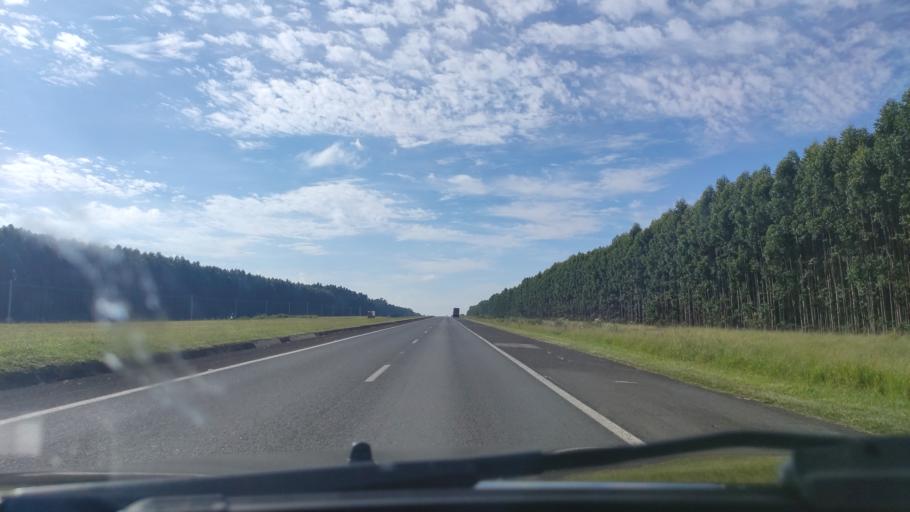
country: BR
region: Sao Paulo
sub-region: Itatinga
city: Itatinga
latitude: -23.0259
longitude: -48.6589
